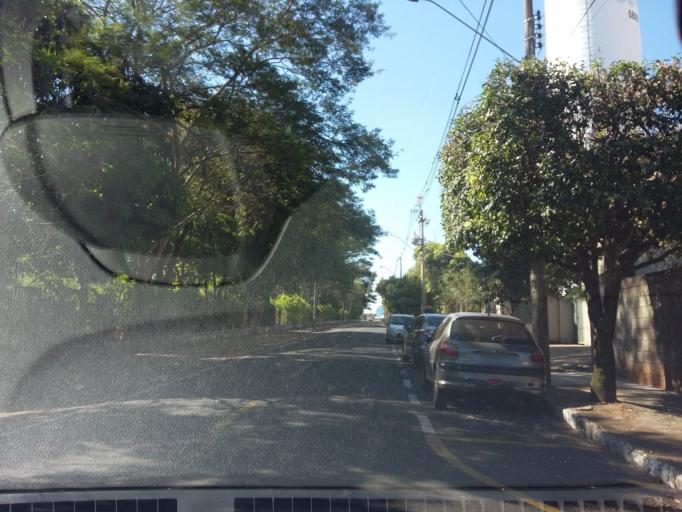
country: BR
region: Sao Paulo
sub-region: Sao Jose Do Rio Preto
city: Sao Jose do Rio Preto
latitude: -20.8354
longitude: -49.3617
